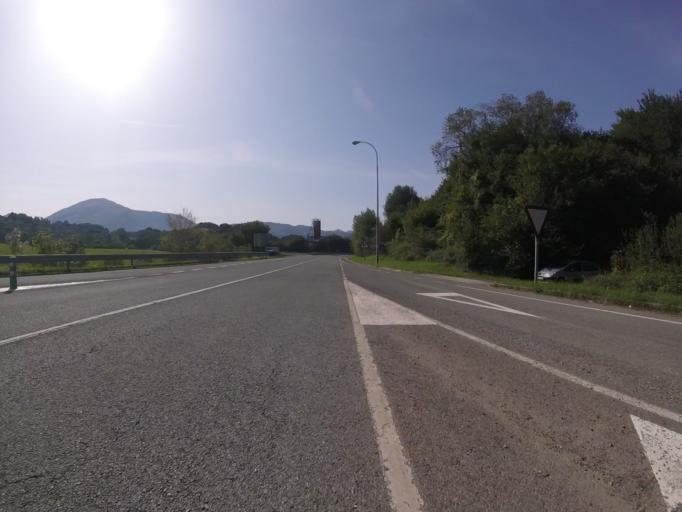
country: ES
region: Navarre
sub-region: Provincia de Navarra
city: Zugarramurdi
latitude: 43.1956
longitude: -1.4837
